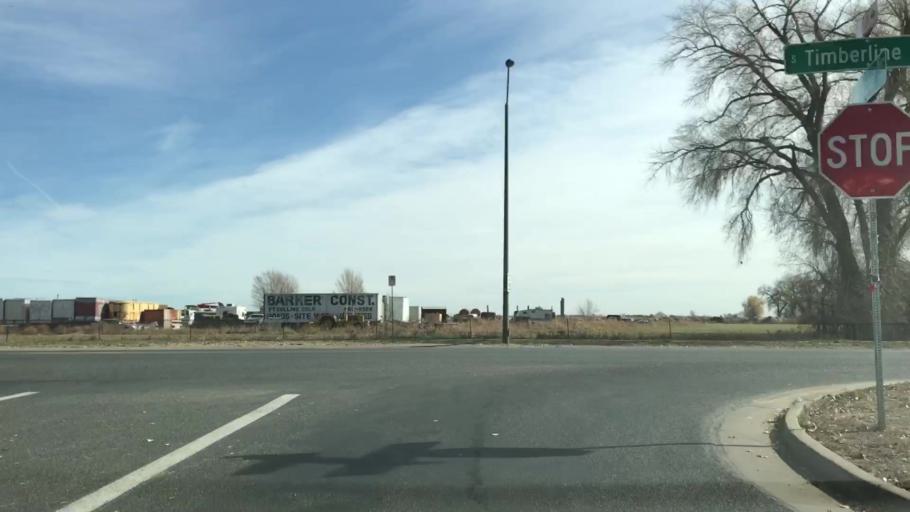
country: US
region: Colorado
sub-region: Larimer County
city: Fort Collins
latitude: 40.5880
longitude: -105.0299
